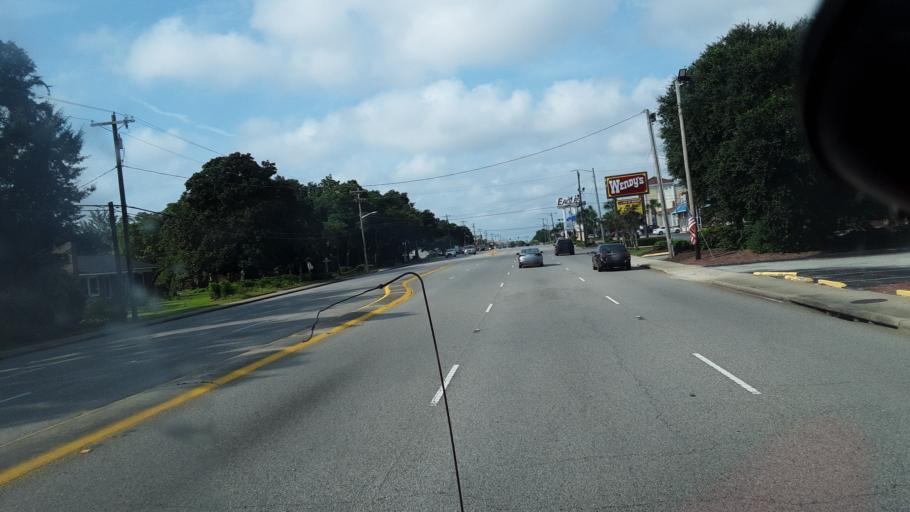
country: US
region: South Carolina
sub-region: Horry County
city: Myrtle Beach
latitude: 33.7125
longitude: -78.8592
